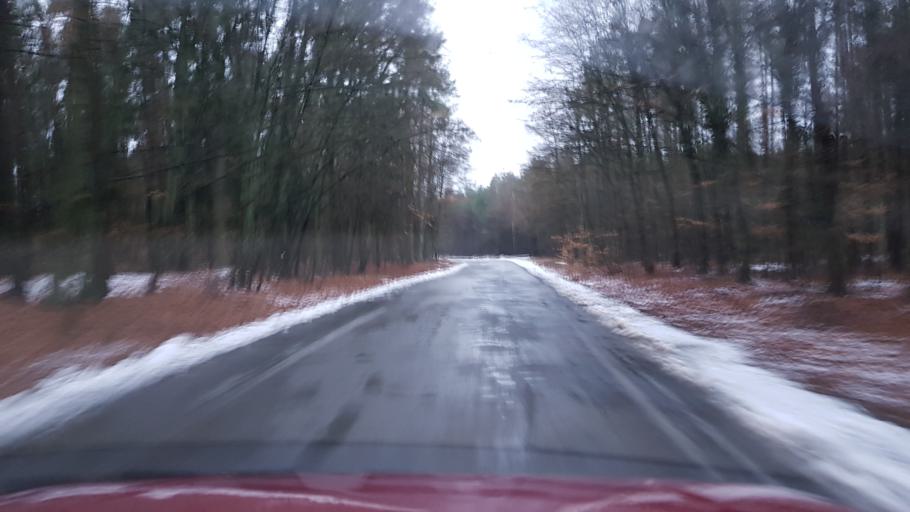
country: PL
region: West Pomeranian Voivodeship
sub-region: Powiat goleniowski
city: Goleniow
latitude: 53.4955
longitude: 14.8834
